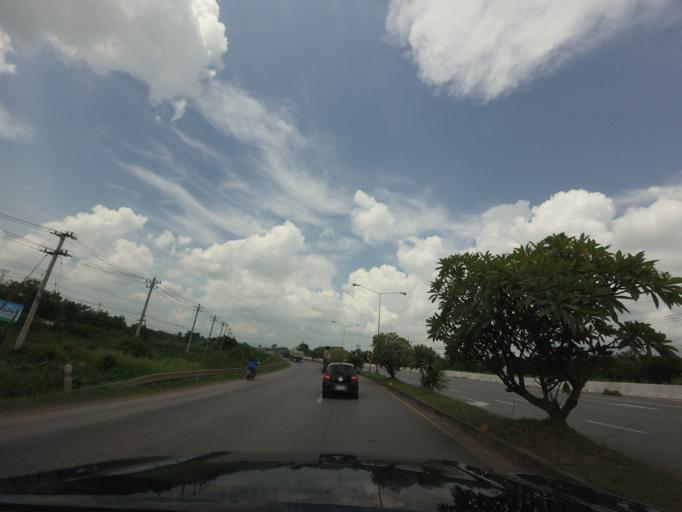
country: TH
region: Khon Kaen
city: Nong Ruea
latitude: 16.4924
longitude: 102.4280
